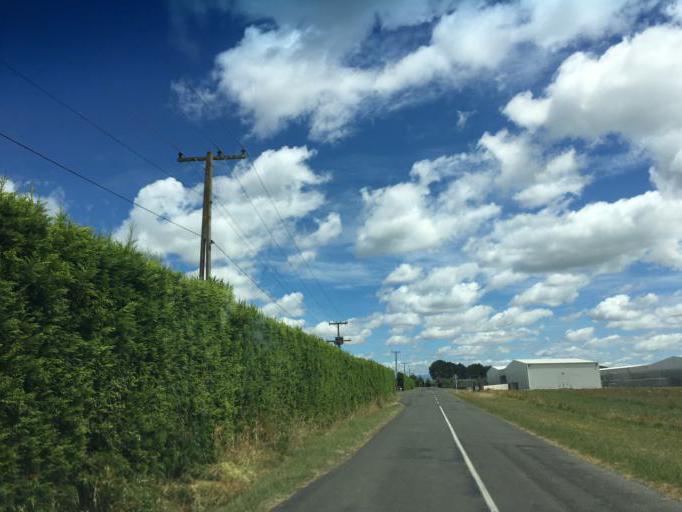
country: NZ
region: Hawke's Bay
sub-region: Hastings District
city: Hastings
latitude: -39.6563
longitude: 176.8913
